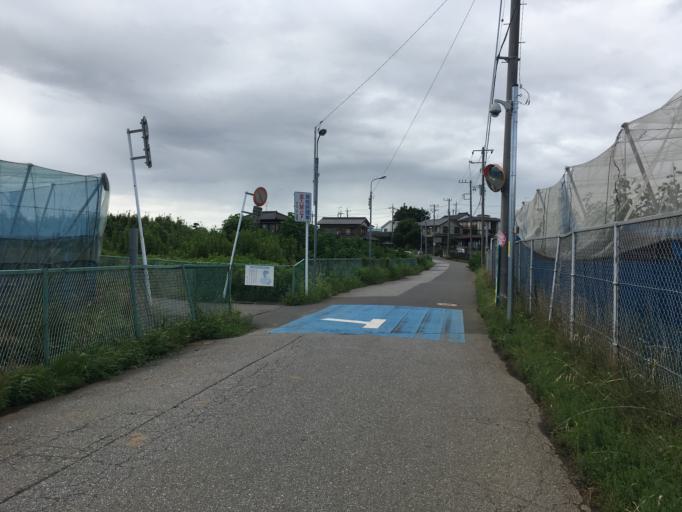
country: JP
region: Chiba
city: Shiroi
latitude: 35.7871
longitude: 139.9978
